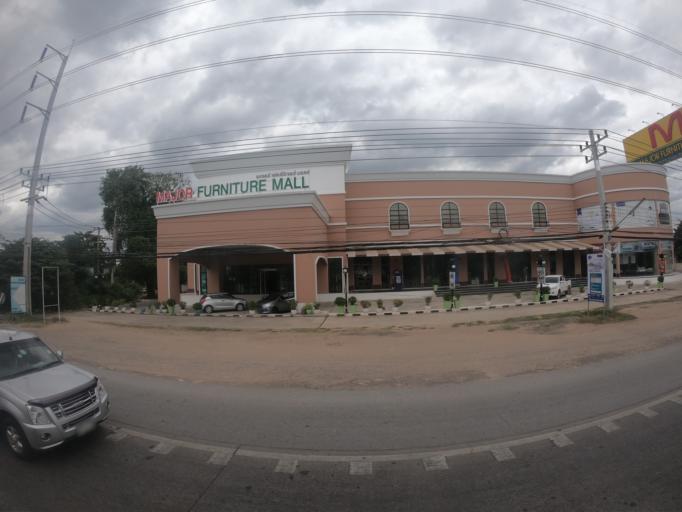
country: TH
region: Nakhon Ratchasima
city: Nakhon Ratchasima
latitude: 14.9263
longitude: 102.1415
